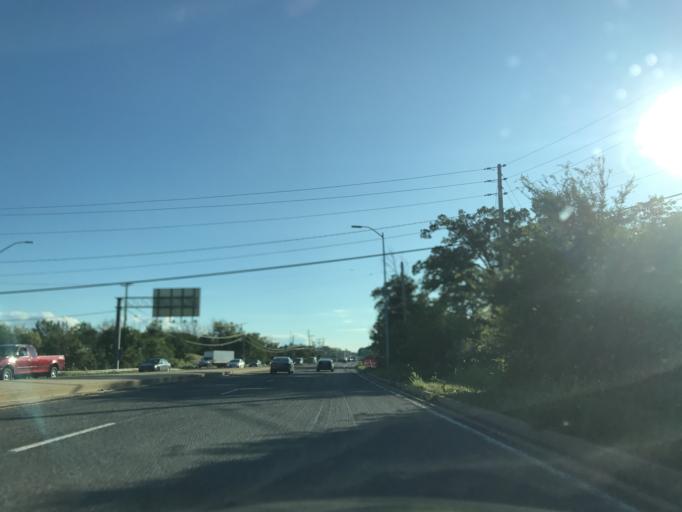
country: US
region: Maryland
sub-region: Howard County
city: Hanover
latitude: 39.1876
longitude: -76.7587
